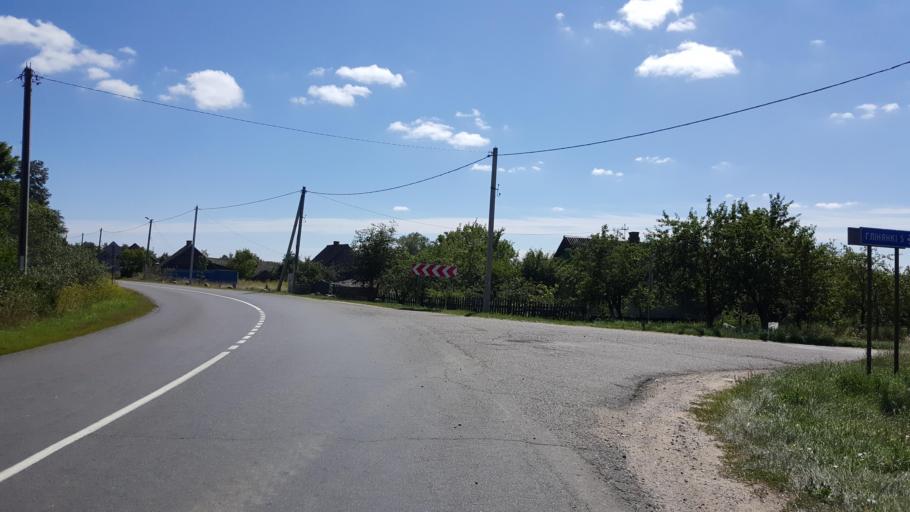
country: BY
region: Brest
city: Kobryn
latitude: 52.3472
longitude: 24.2008
